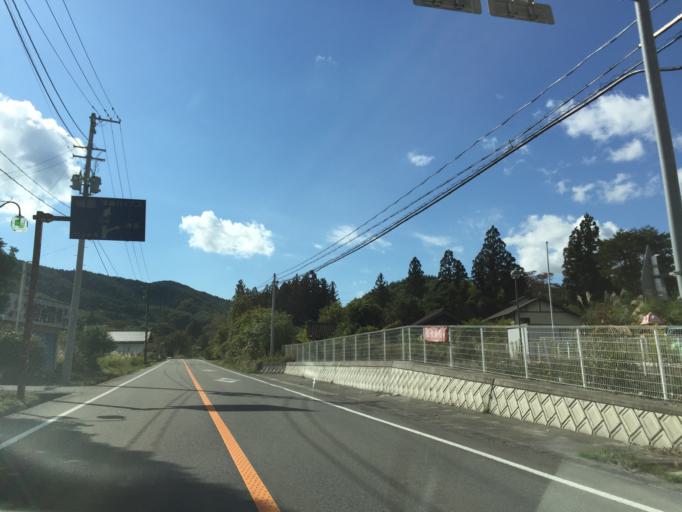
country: JP
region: Fukushima
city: Funehikimachi-funehiki
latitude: 37.5602
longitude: 140.7630
